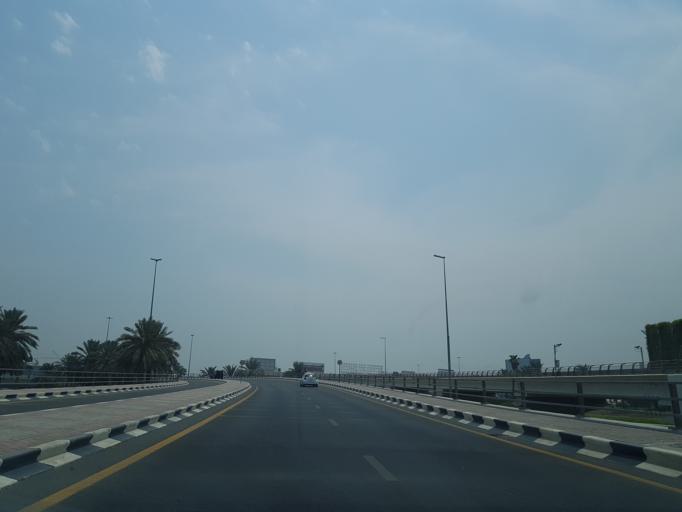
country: AE
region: Ash Shariqah
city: Sharjah
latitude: 25.2496
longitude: 55.3341
